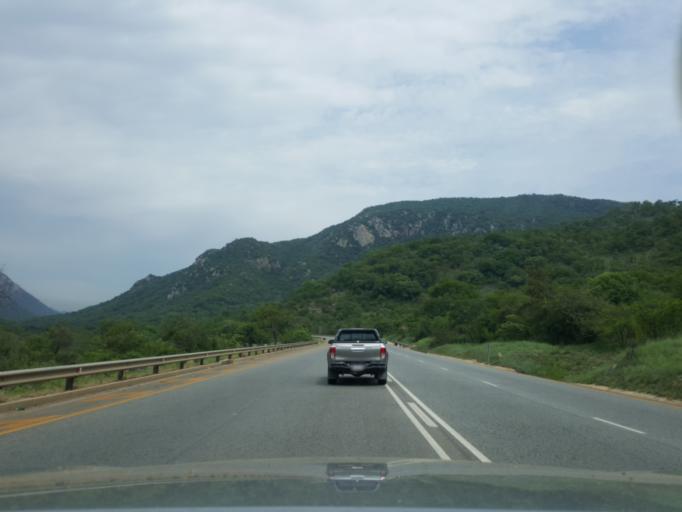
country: SZ
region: Hhohho
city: Ntfonjeni
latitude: -25.5313
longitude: 31.2861
